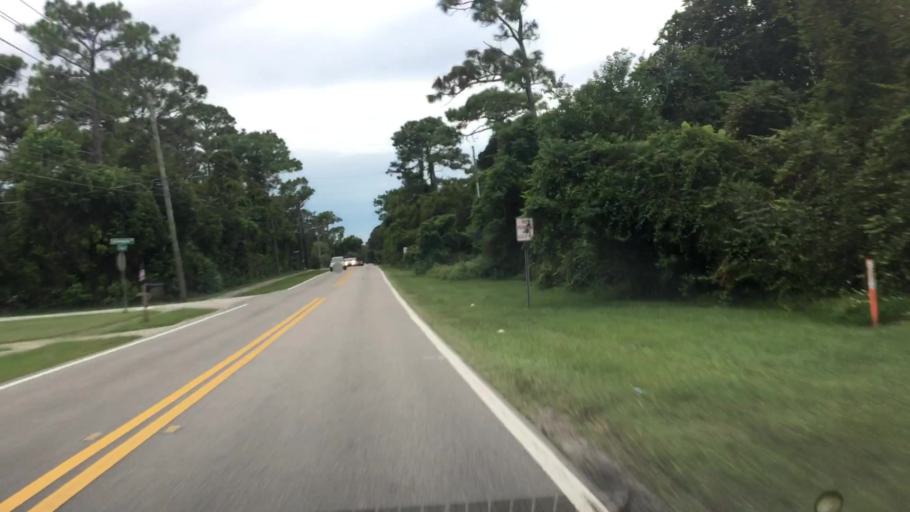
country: US
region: Florida
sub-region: Volusia County
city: DeBary
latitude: 28.8903
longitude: -81.2952
